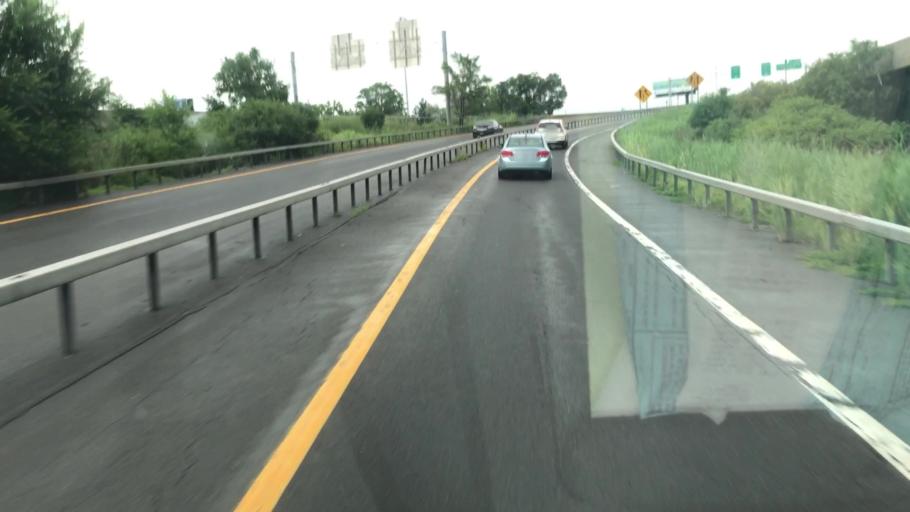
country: US
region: New York
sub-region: Onondaga County
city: Galeville
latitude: 43.0762
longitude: -76.1748
